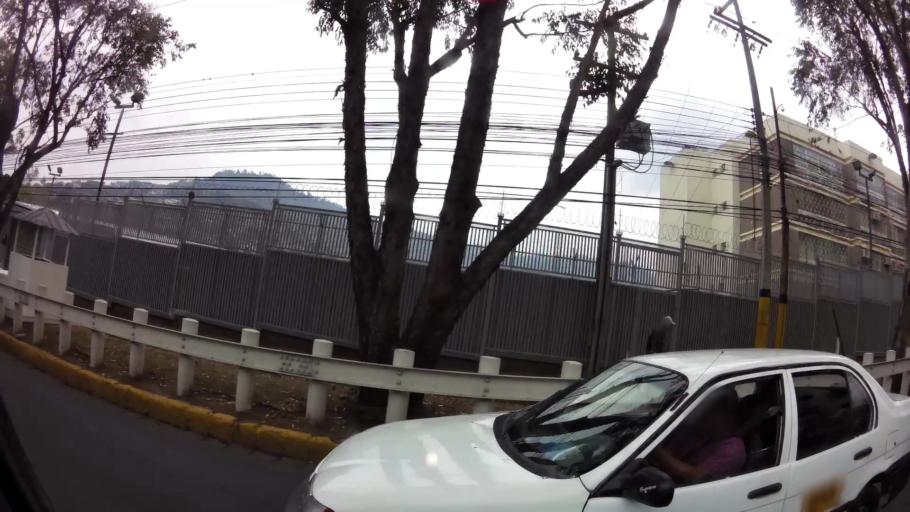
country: HN
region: Francisco Morazan
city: Tegucigalpa
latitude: 14.1037
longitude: -87.1901
